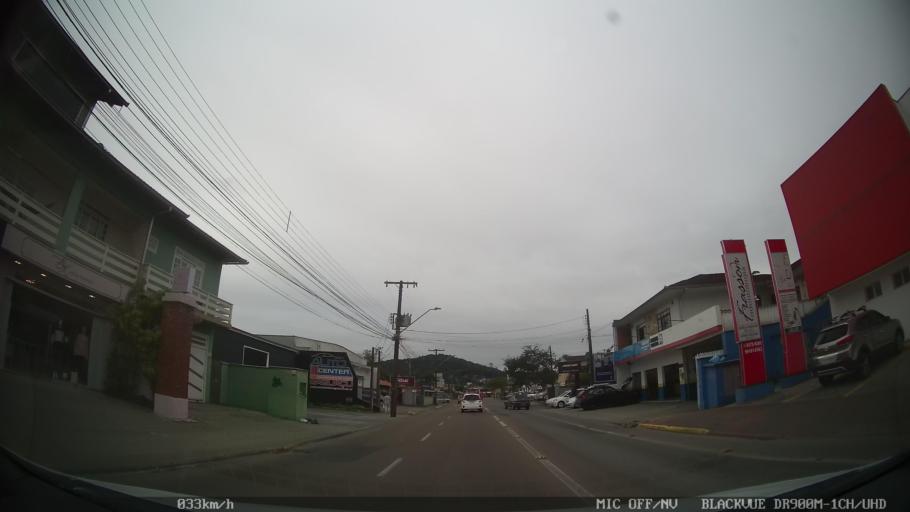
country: BR
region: Santa Catarina
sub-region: Joinville
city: Joinville
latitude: -26.2803
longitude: -48.8340
